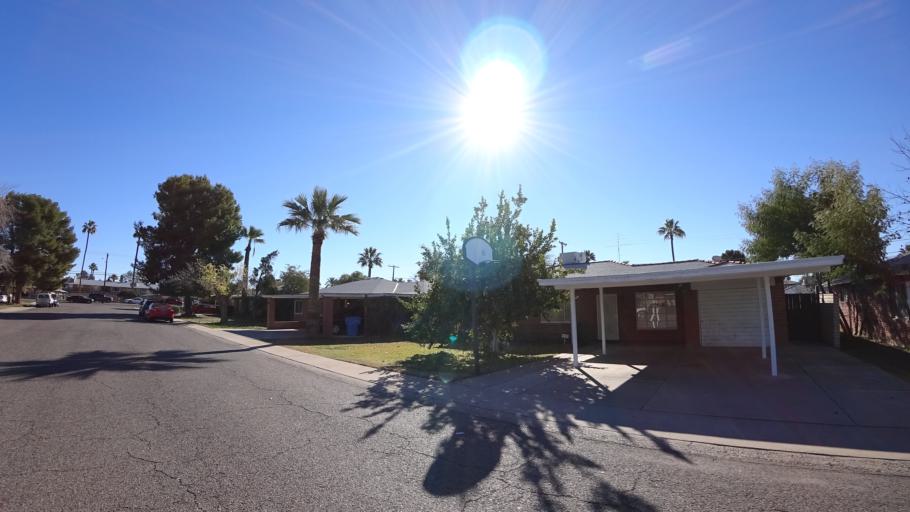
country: US
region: Arizona
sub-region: Maricopa County
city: Phoenix
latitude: 33.4995
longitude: -112.0269
